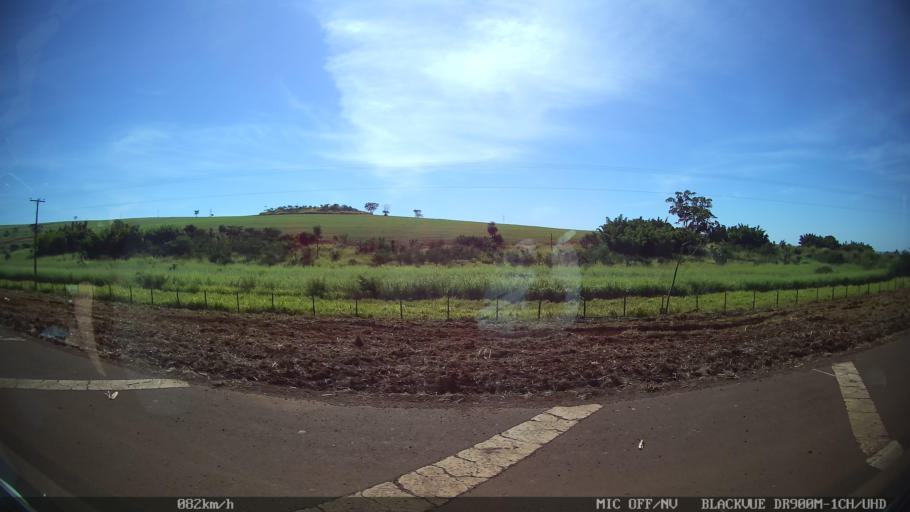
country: BR
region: Sao Paulo
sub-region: Ipua
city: Ipua
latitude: -20.4926
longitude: -48.0082
